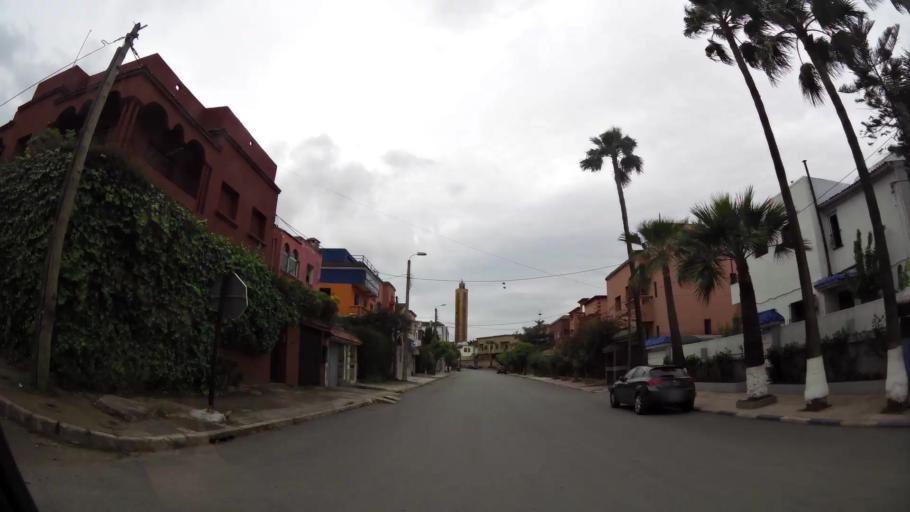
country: MA
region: Grand Casablanca
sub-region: Mediouna
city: Tit Mellil
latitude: 33.5655
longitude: -7.5330
